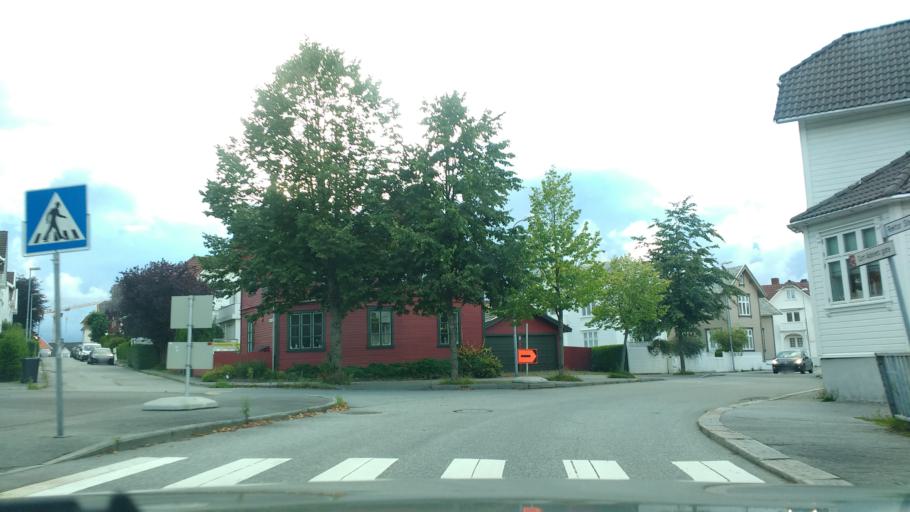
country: NO
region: Rogaland
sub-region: Stavanger
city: Stavanger
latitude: 58.9620
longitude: 5.7307
